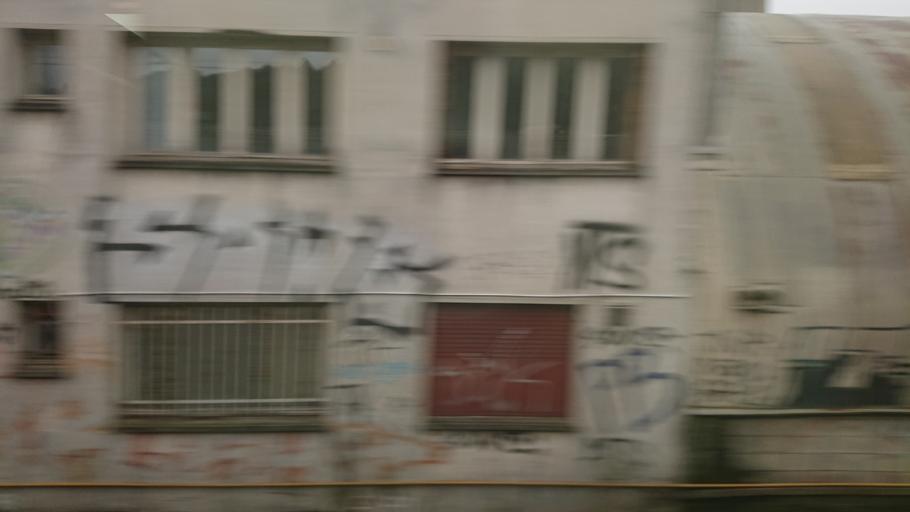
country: FR
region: Rhone-Alpes
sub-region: Departement de la Savoie
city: Brison-Saint-Innocent
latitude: 45.7095
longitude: 5.8918
